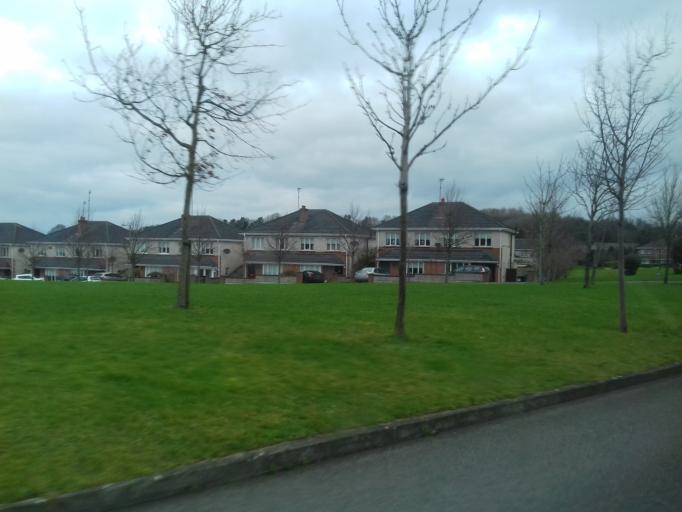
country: IE
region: Leinster
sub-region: An Mhi
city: Duleek
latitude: 53.6911
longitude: -6.4126
